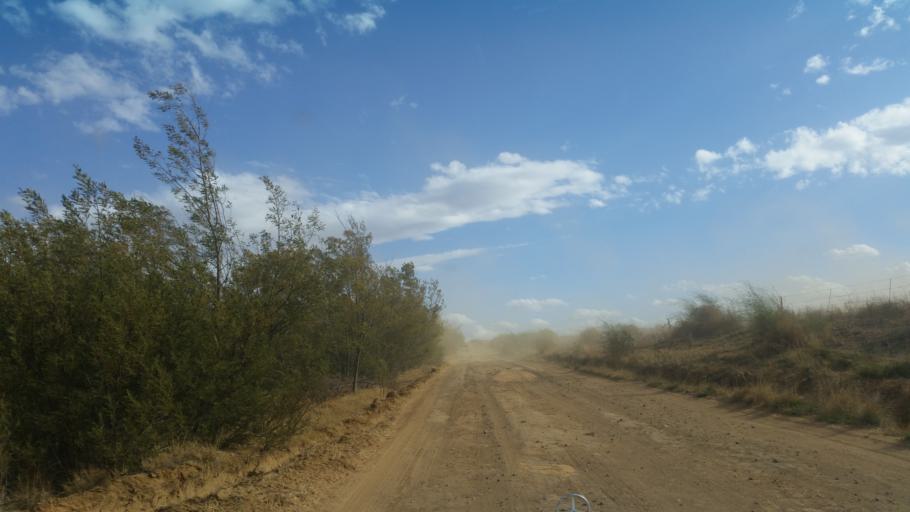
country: ZA
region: Orange Free State
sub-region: Thabo Mofutsanyana District Municipality
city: Phuthaditjhaba
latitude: -28.3633
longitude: 28.5996
